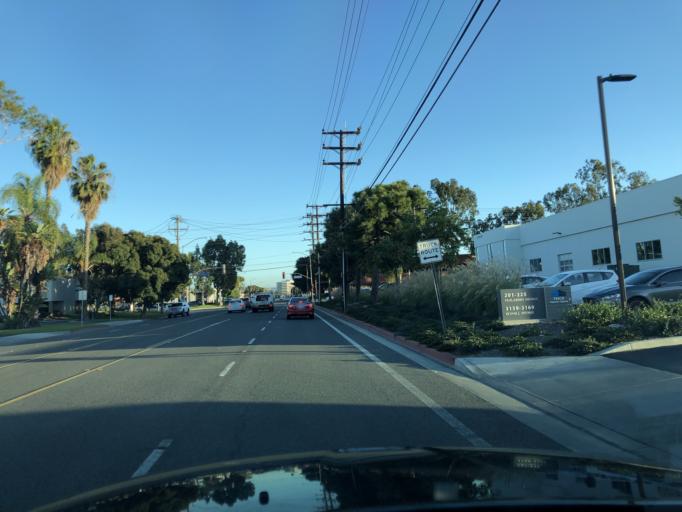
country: US
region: California
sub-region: Orange County
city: Irvine
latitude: 33.6805
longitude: -117.8750
